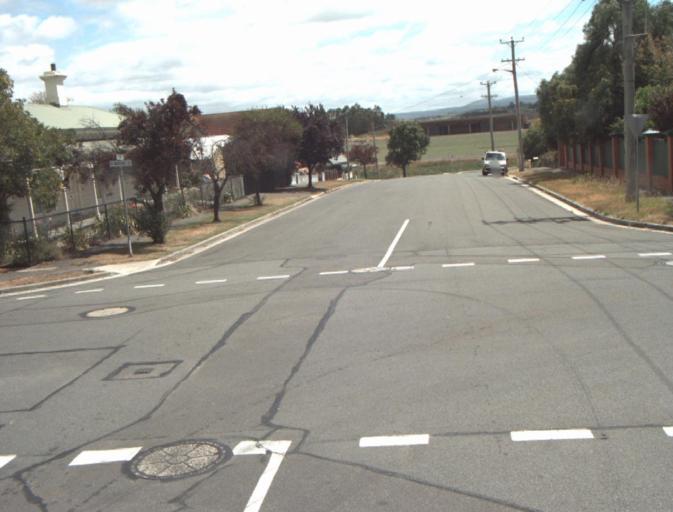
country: AU
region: Tasmania
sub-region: Launceston
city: Launceston
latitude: -41.4220
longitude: 147.1285
